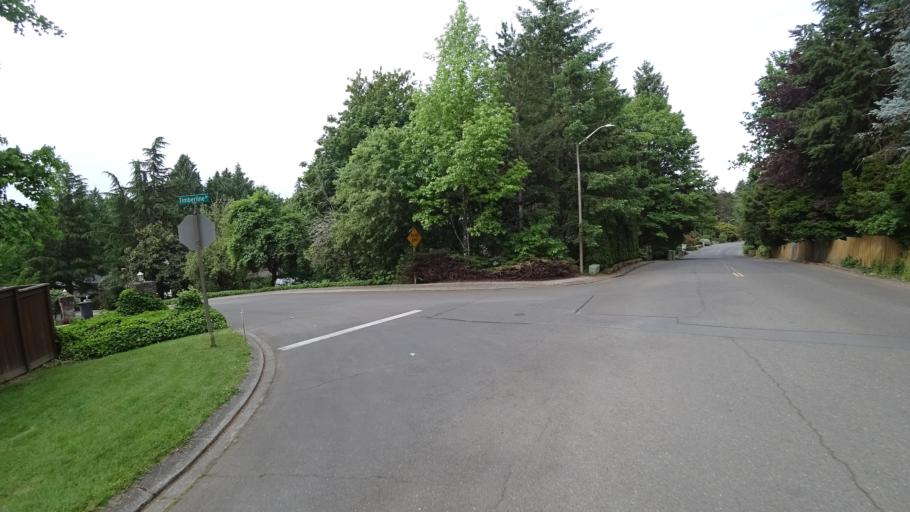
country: US
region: Oregon
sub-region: Clackamas County
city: Lake Oswego
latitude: 45.4302
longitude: -122.6839
